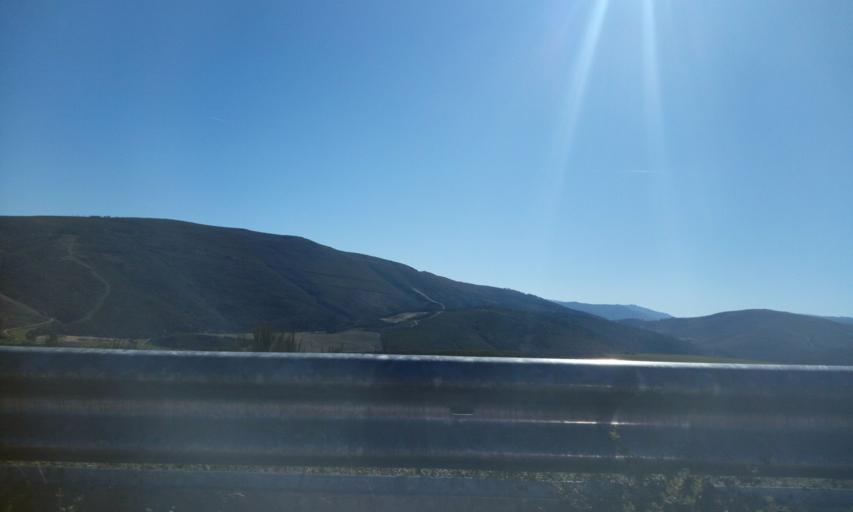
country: PT
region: Guarda
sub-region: Manteigas
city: Manteigas
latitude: 40.4629
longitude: -7.5018
